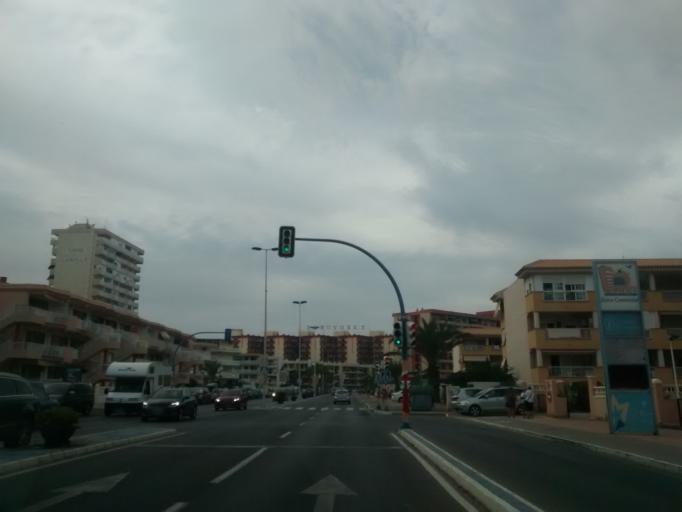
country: ES
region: Murcia
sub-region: Murcia
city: La Manga del Mar Menor
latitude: 37.6792
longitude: -0.7337
